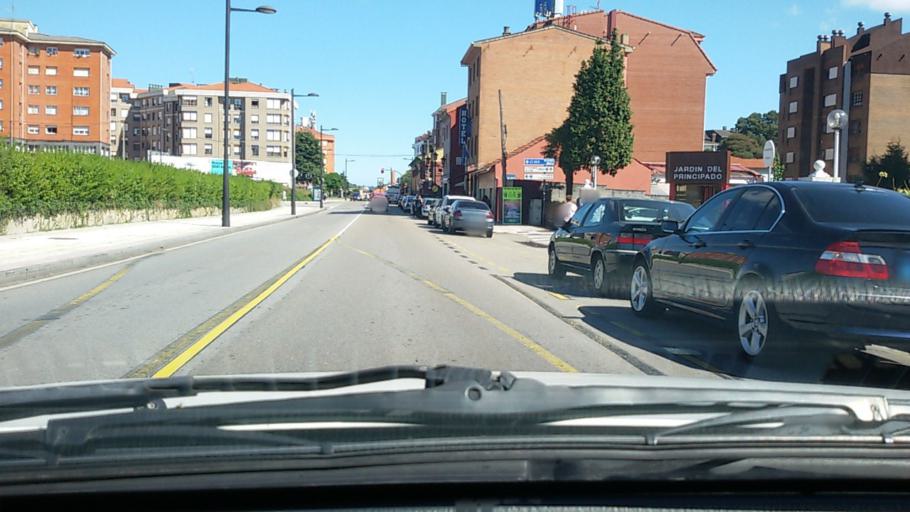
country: ES
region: Asturias
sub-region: Province of Asturias
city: Lugones
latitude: 43.3831
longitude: -5.8266
